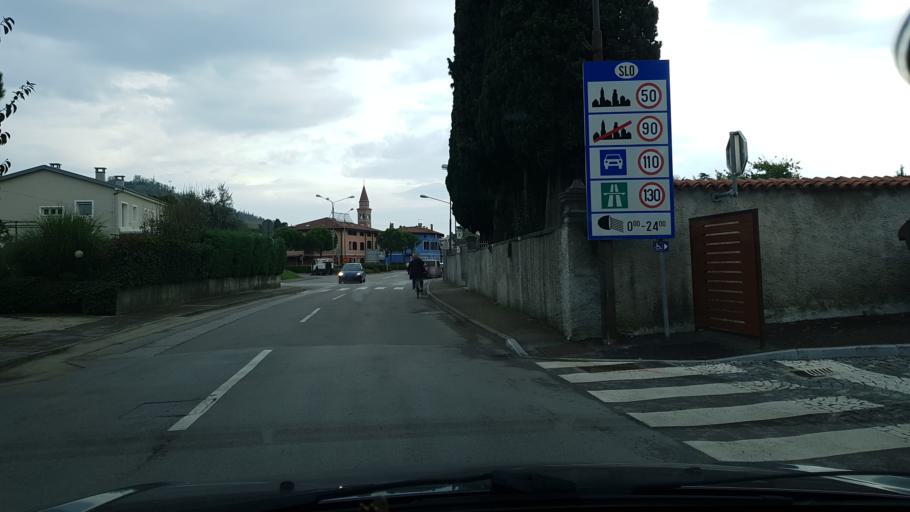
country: SI
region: Sempeter-Vrtojba
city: Sempeter pri Gorici
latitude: 45.9321
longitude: 13.6362
